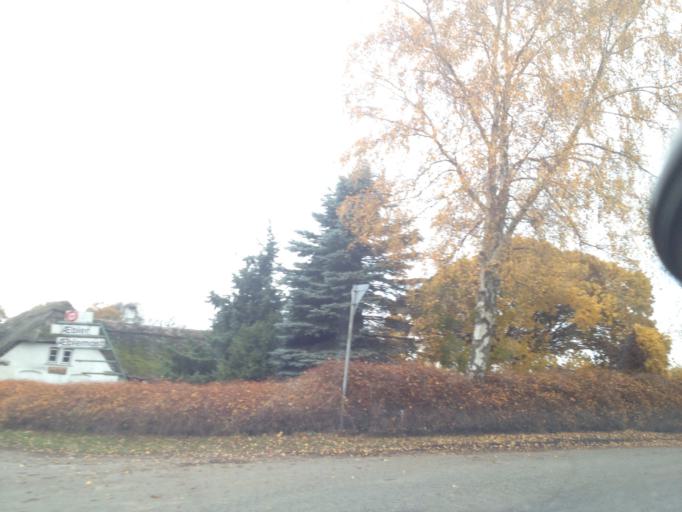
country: DK
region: South Denmark
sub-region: Assens Kommune
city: Vissenbjerg
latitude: 55.4109
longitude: 10.1528
